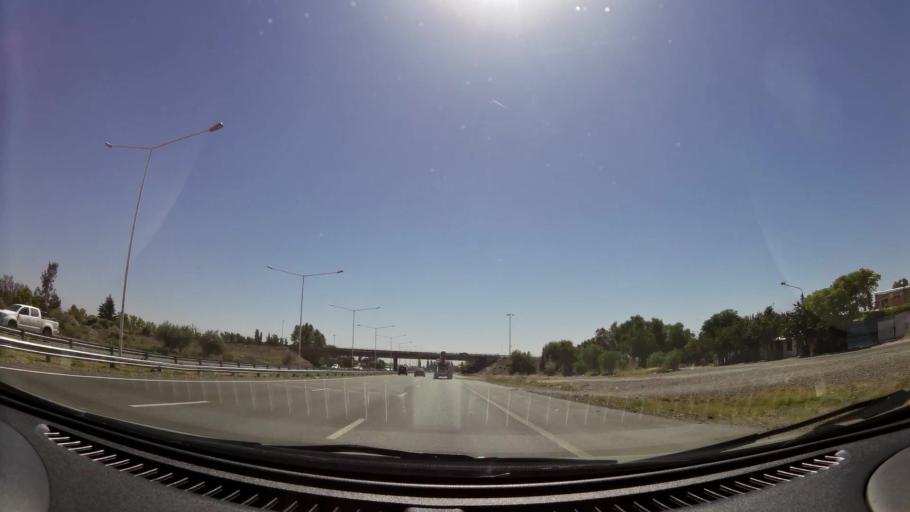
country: AR
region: Mendoza
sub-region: Departamento de Godoy Cruz
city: Godoy Cruz
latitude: -32.9546
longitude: -68.8350
